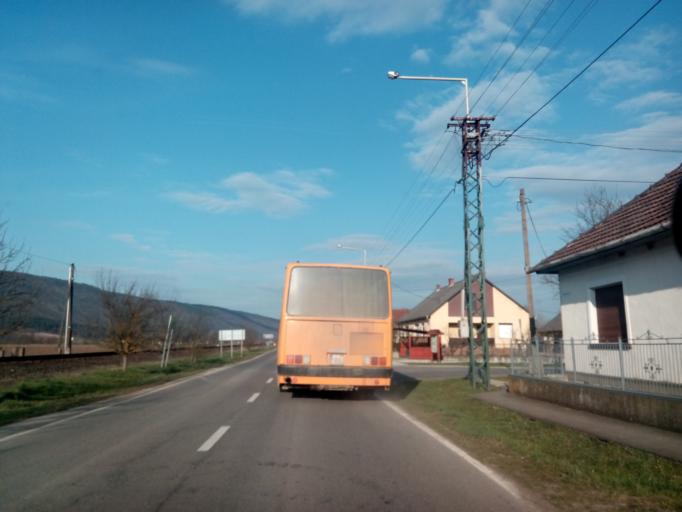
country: HU
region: Borsod-Abauj-Zemplen
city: Szendro
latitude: 48.5473
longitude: 20.7597
